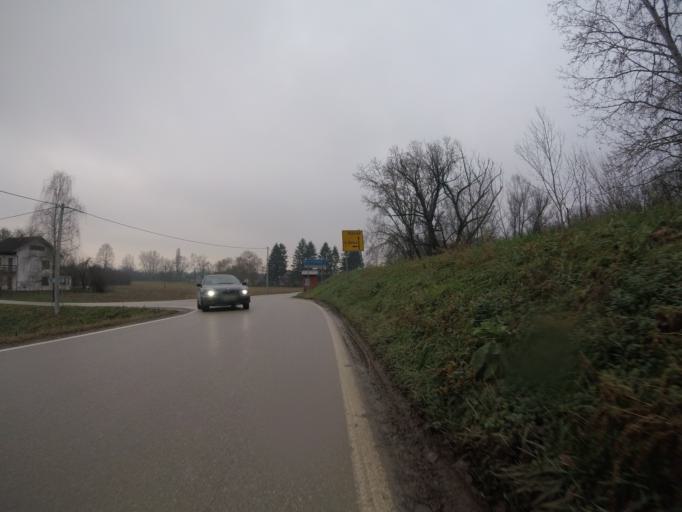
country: HR
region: Zagrebacka
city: Kuce
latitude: 45.7018
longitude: 16.2120
